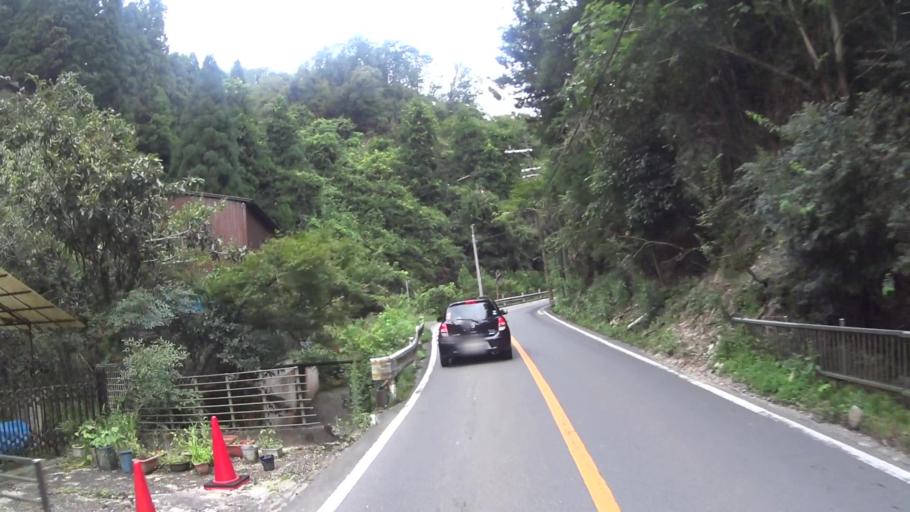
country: JP
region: Kyoto
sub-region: Kyoto-shi
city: Kamigyo-ku
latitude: 35.0353
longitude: 135.8097
